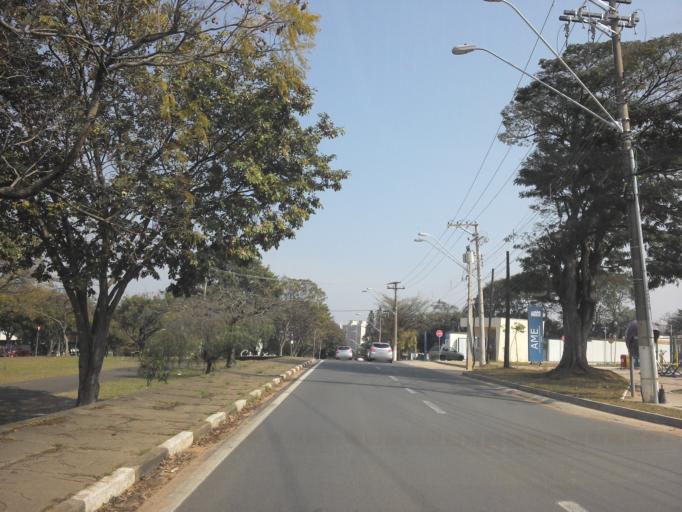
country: BR
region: Sao Paulo
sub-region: Campinas
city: Campinas
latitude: -22.9162
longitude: -47.0699
